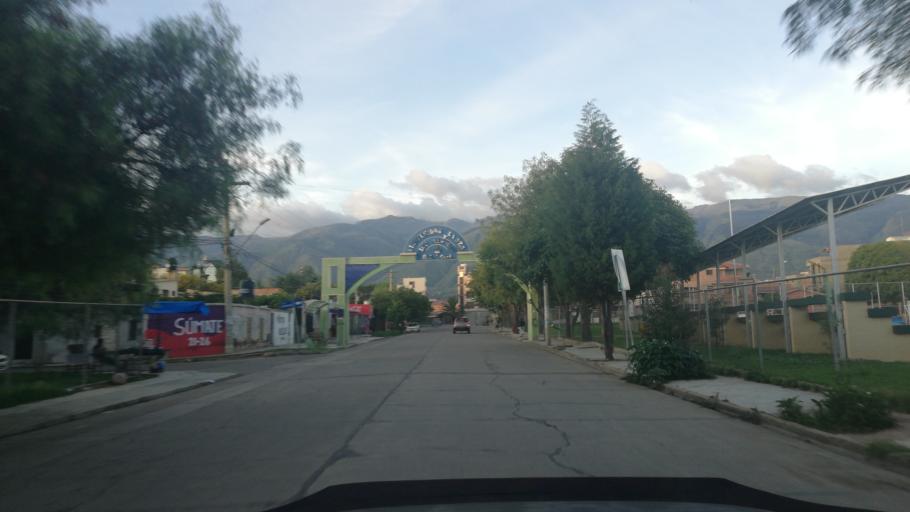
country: BO
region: Cochabamba
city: Cochabamba
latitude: -17.3751
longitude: -66.1874
